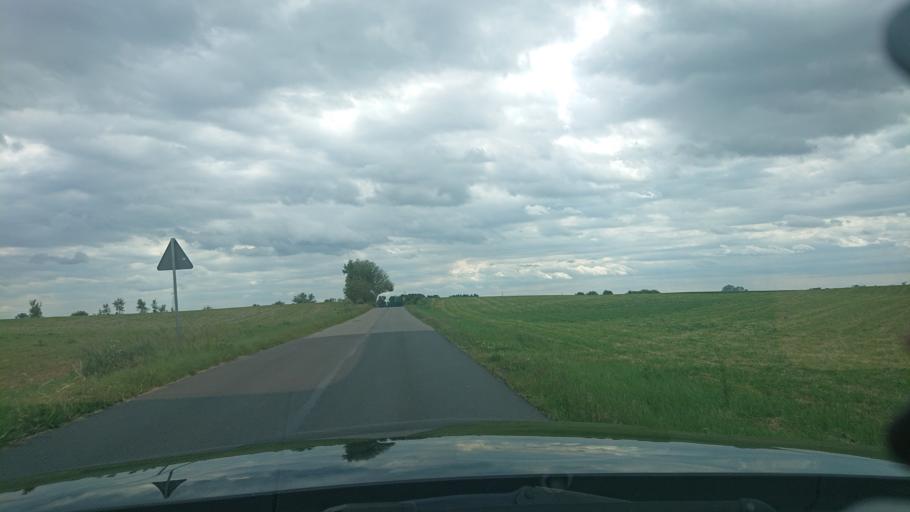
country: PL
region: Greater Poland Voivodeship
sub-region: Powiat gnieznienski
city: Gniezno
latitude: 52.5398
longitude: 17.5362
